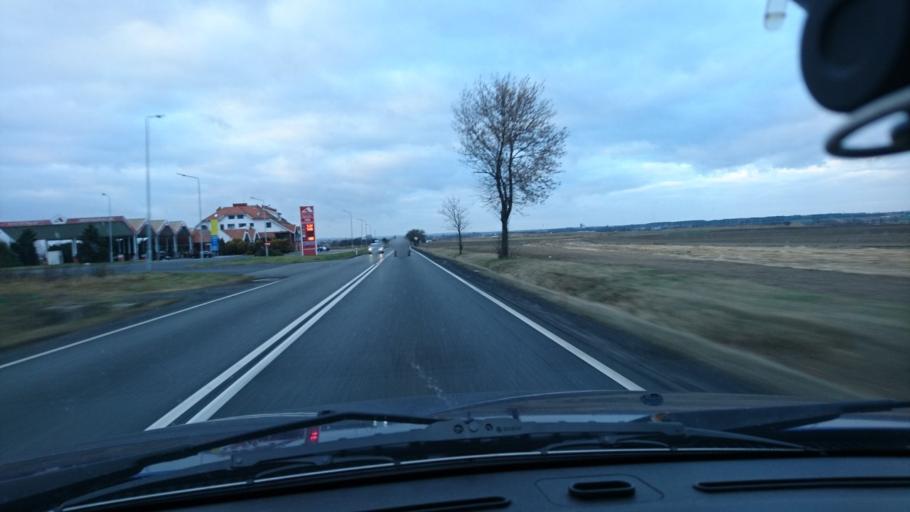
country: PL
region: Greater Poland Voivodeship
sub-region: Powiat kepinski
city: Baranow
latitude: 51.2488
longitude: 18.0165
